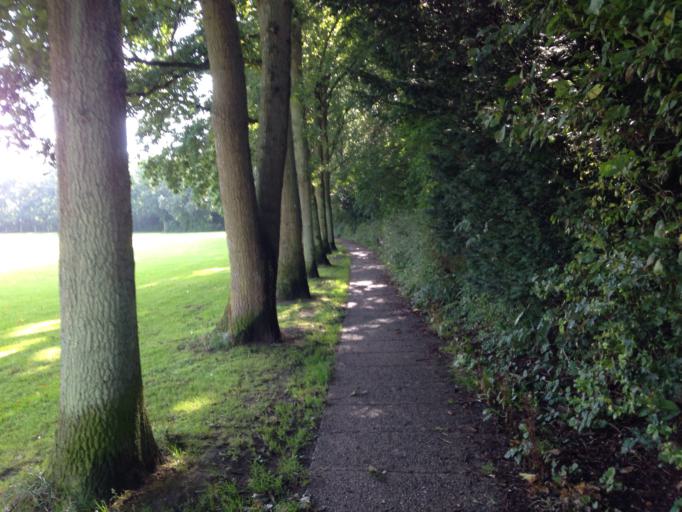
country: DK
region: Capital Region
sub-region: Glostrup Kommune
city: Glostrup
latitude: 55.6694
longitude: 12.3870
